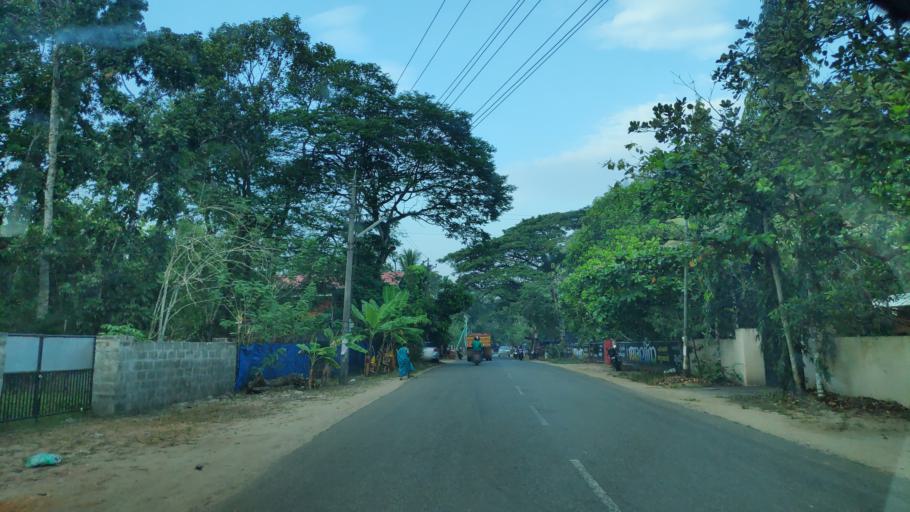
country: IN
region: Kerala
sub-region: Alappuzha
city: Shertallai
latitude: 9.6537
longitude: 76.3746
